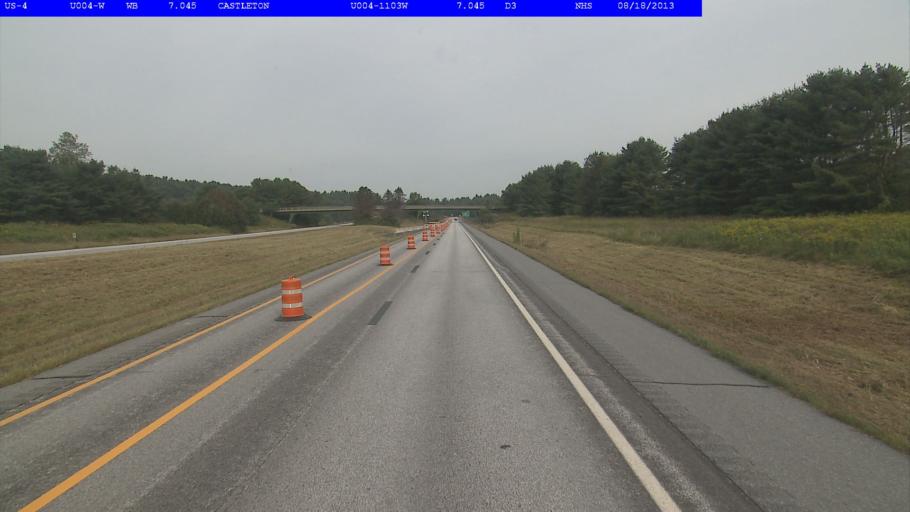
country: US
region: Vermont
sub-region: Rutland County
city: Castleton
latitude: 43.6183
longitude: -73.1791
